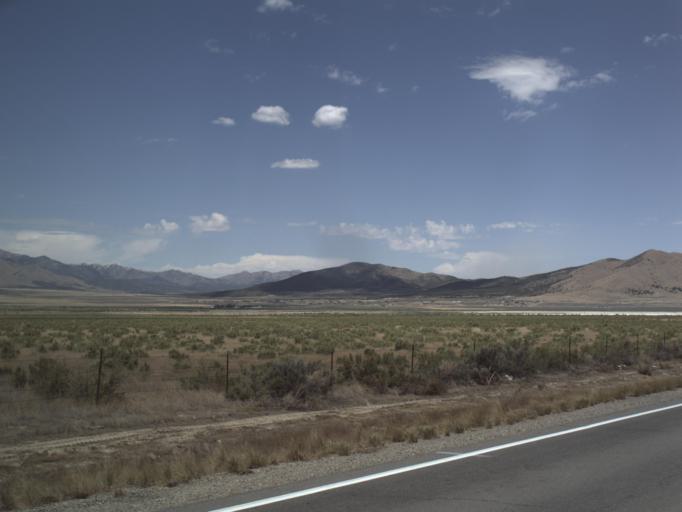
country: US
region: Utah
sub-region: Tooele County
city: Tooele
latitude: 40.3910
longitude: -112.3862
